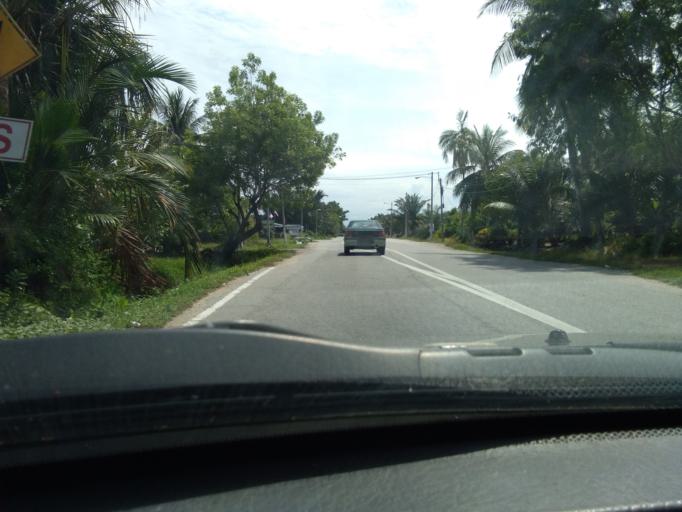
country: MY
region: Perak
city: Bagan Serai
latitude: 5.0209
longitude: 100.5478
